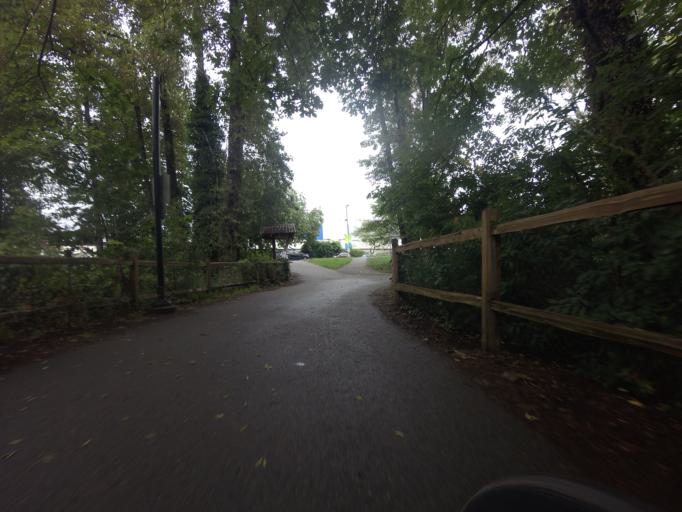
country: CA
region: British Columbia
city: West End
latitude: 49.3237
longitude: -123.1395
